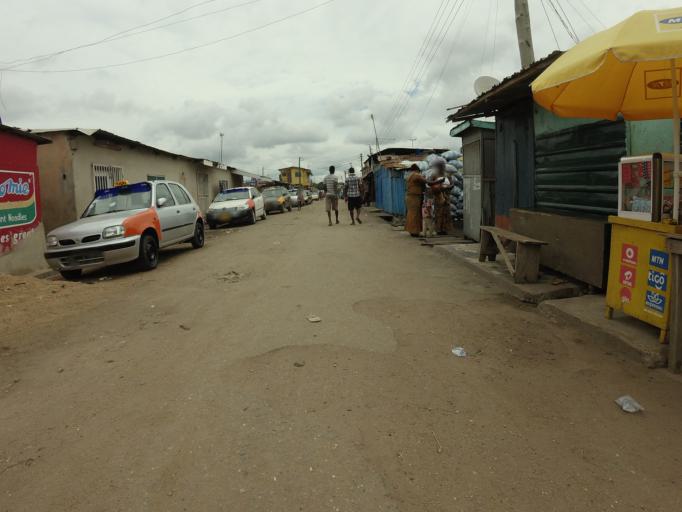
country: GH
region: Greater Accra
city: Accra
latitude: 5.5951
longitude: -0.2146
